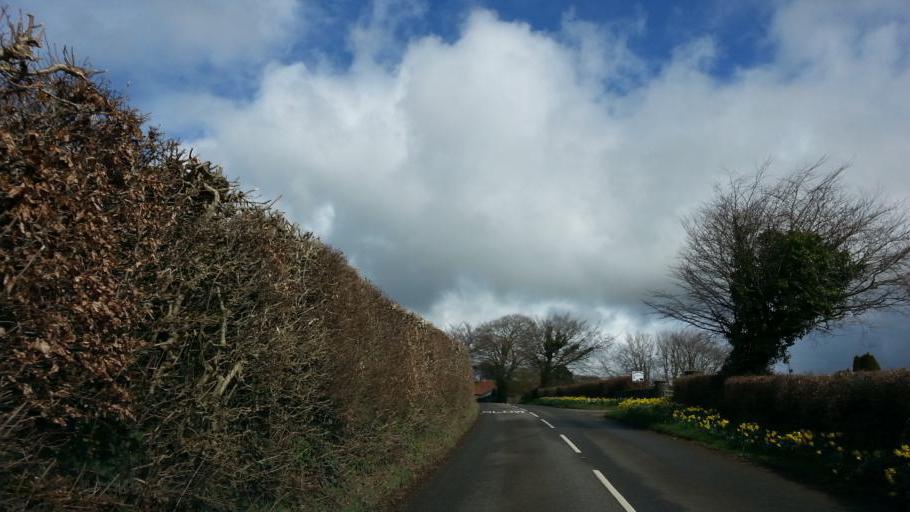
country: GB
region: England
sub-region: Devon
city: Barnstaple
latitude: 51.1082
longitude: -4.0213
